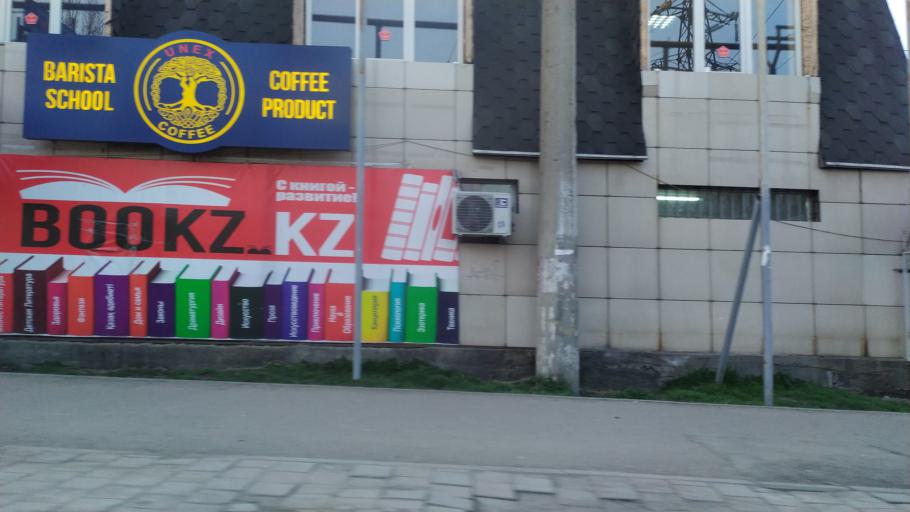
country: KZ
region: Almaty Qalasy
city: Almaty
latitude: 43.2222
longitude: 76.8839
